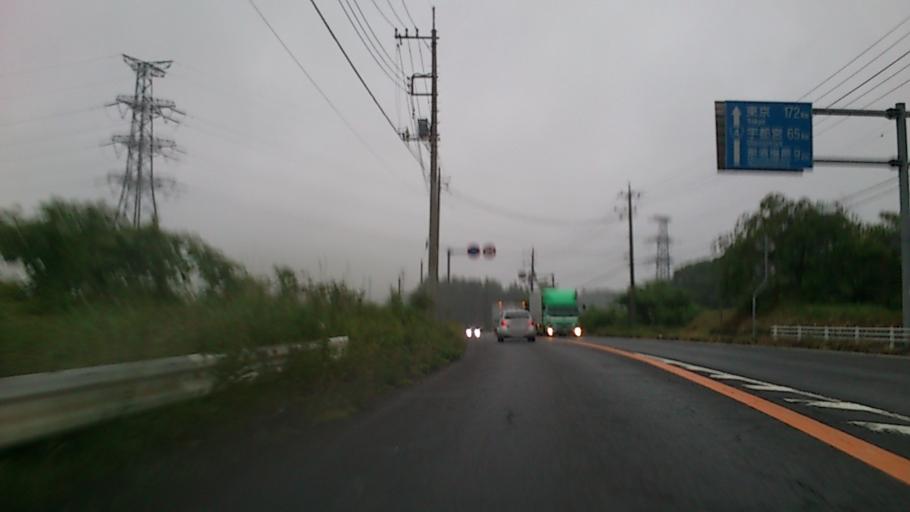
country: JP
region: Tochigi
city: Kuroiso
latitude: 37.0360
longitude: 140.0953
